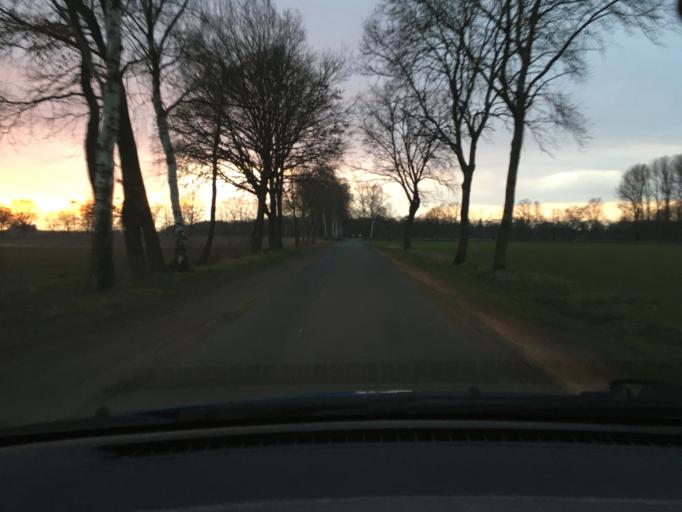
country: DE
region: Lower Saxony
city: Neetze
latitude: 53.3036
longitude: 10.6651
